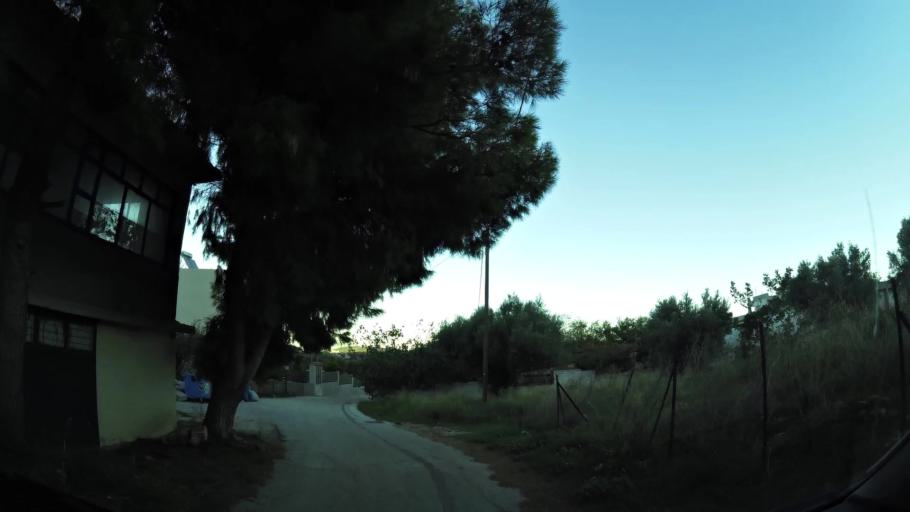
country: GR
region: Attica
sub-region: Nomarchia Anatolikis Attikis
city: Paiania
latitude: 37.9690
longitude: 23.8498
